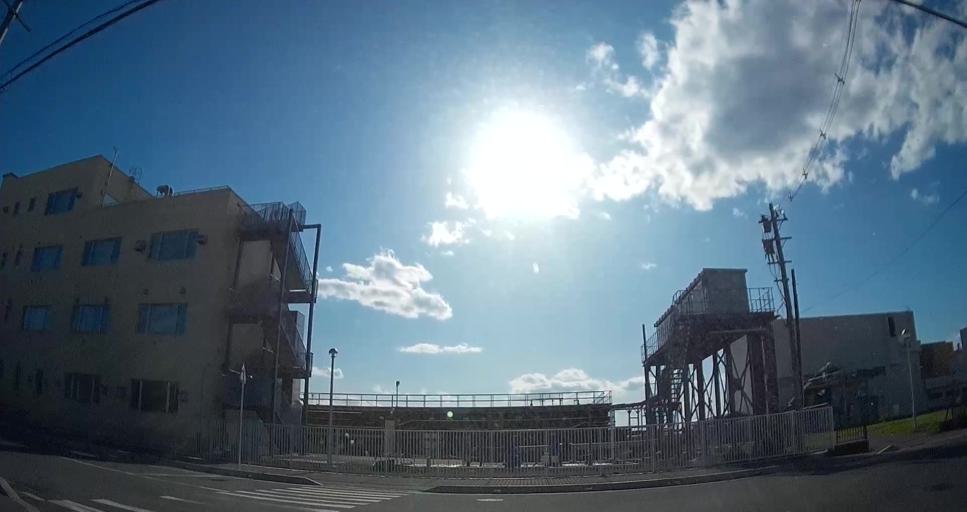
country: JP
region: Miyagi
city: Ishinomaki
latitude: 38.4137
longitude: 141.3169
